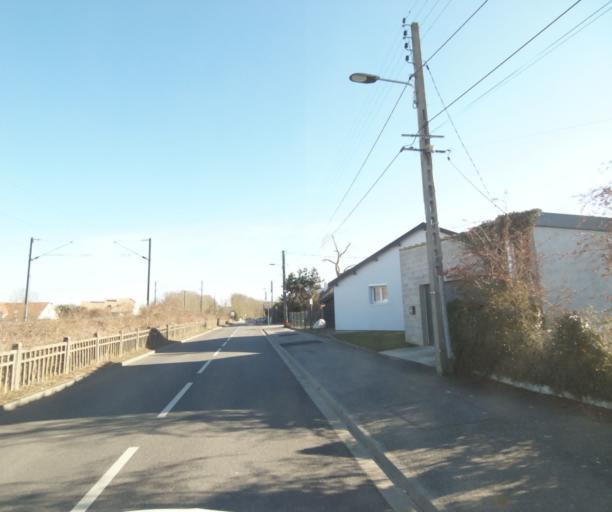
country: FR
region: Lorraine
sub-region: Departement de Meurthe-et-Moselle
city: Laneuveville-devant-Nancy
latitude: 48.6594
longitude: 6.2226
